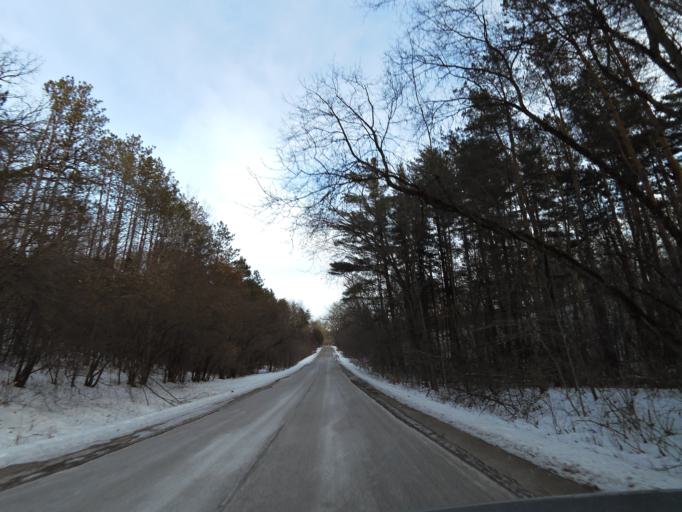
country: US
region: Minnesota
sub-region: Washington County
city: Afton
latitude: 44.9126
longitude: -92.8317
